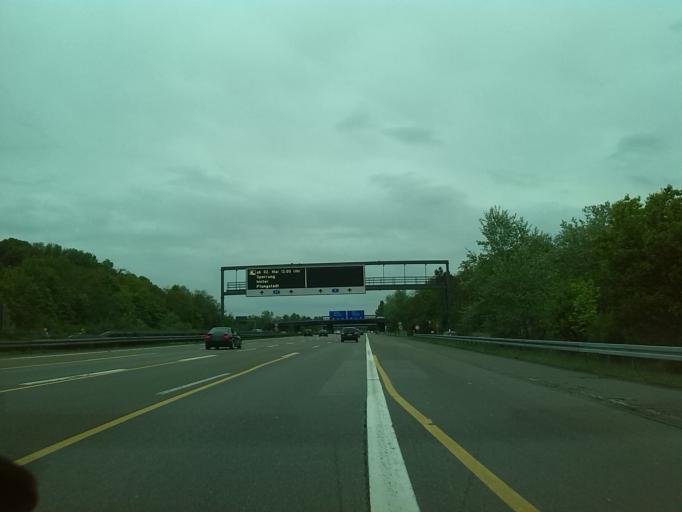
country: DE
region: Hesse
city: Griesheim
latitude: 49.8638
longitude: 8.5991
